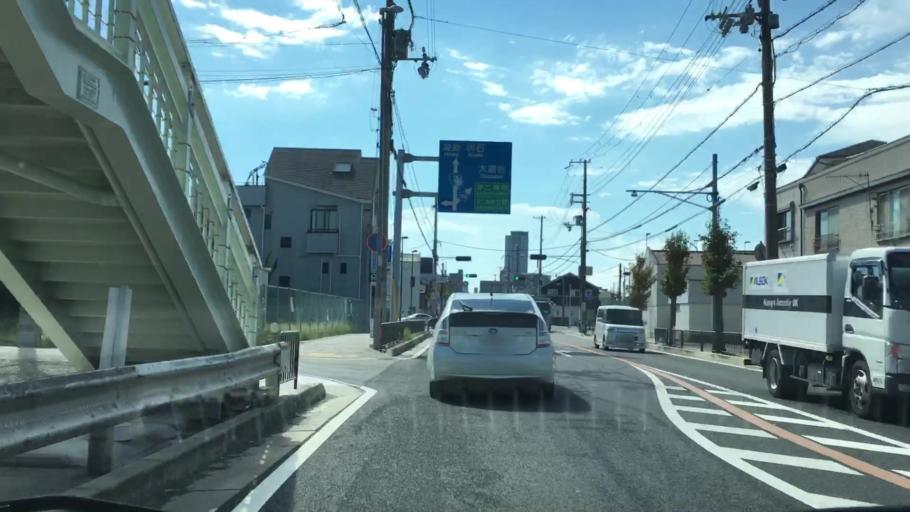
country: JP
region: Hyogo
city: Akashi
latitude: 34.6465
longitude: 135.0073
